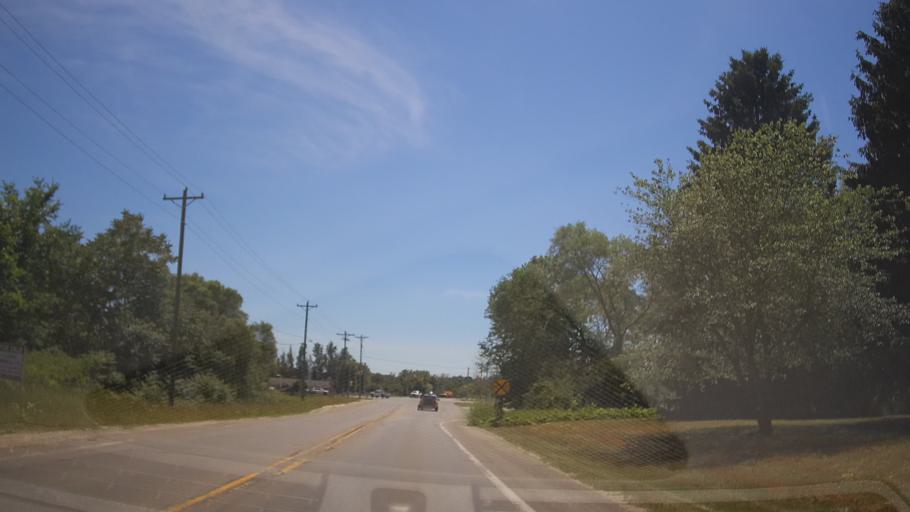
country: US
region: Michigan
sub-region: Grand Traverse County
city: Traverse City
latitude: 44.6669
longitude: -85.6902
